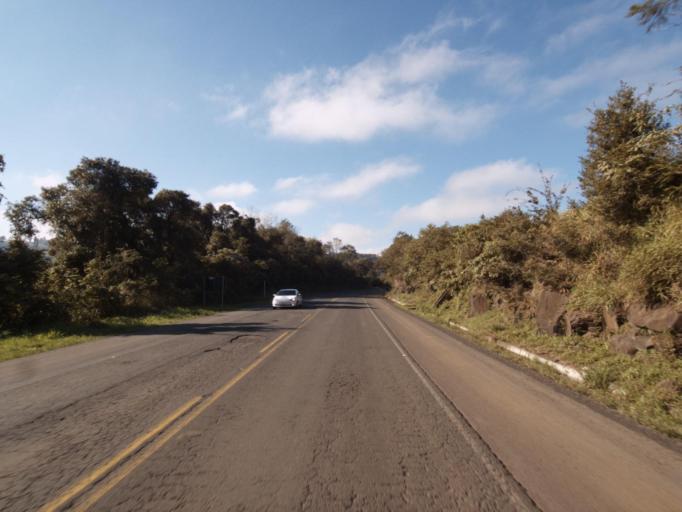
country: BR
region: Rio Grande do Sul
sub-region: Frederico Westphalen
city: Frederico Westphalen
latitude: -27.0599
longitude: -53.2232
